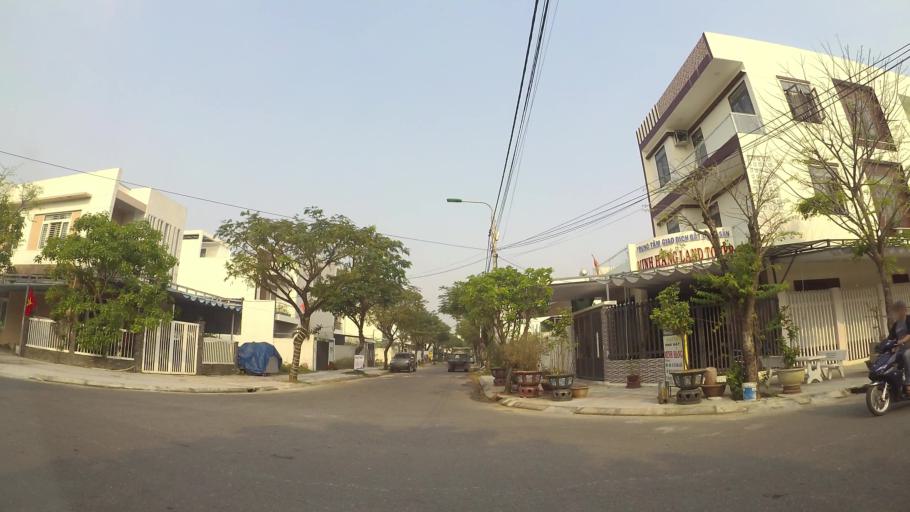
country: VN
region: Da Nang
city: Cam Le
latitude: 16.0055
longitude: 108.2238
